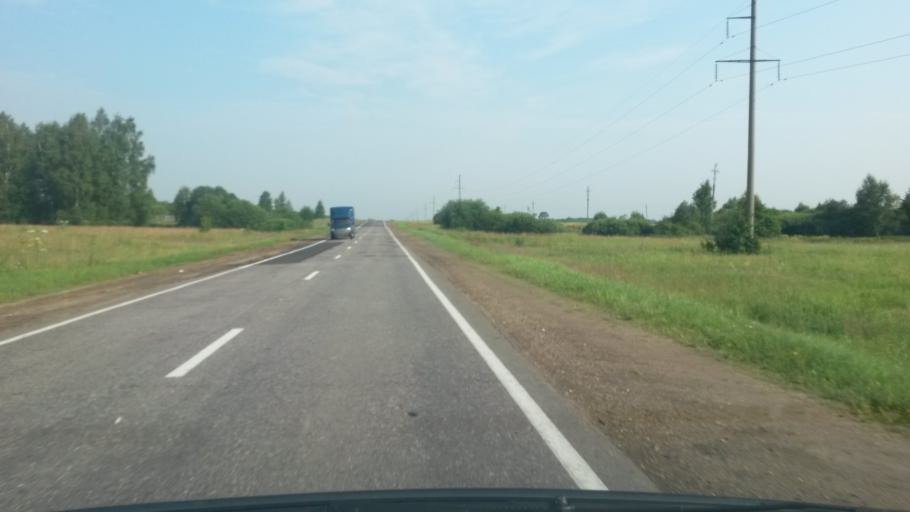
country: RU
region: Jaroslavl
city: Gavrilov-Yam
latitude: 57.3504
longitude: 39.7889
